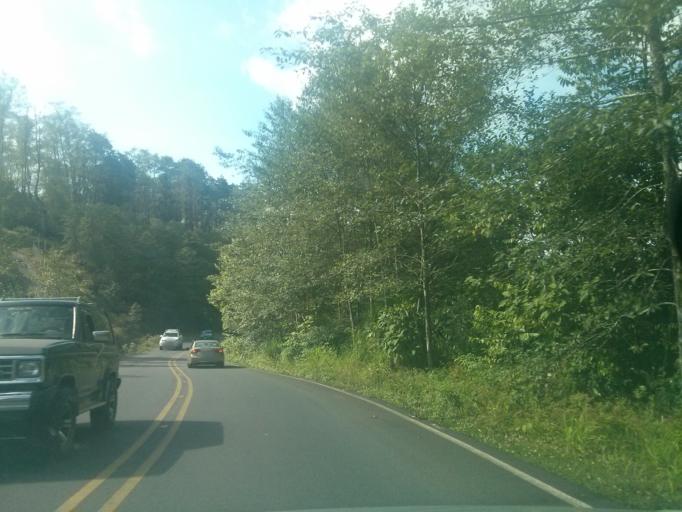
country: CR
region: Heredia
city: Santo Domingo
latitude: 10.1849
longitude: -84.1550
